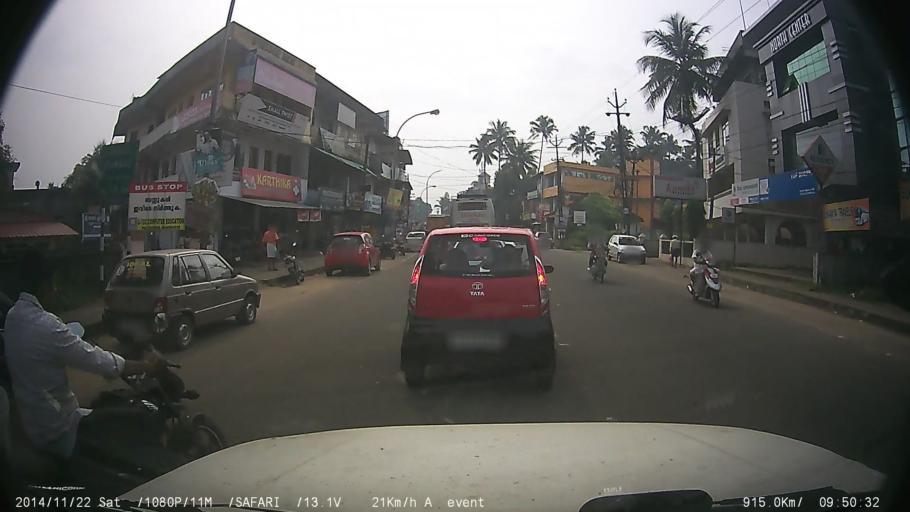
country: IN
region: Kerala
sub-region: Ernakulam
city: Perumpavur
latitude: 10.1182
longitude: 76.4752
